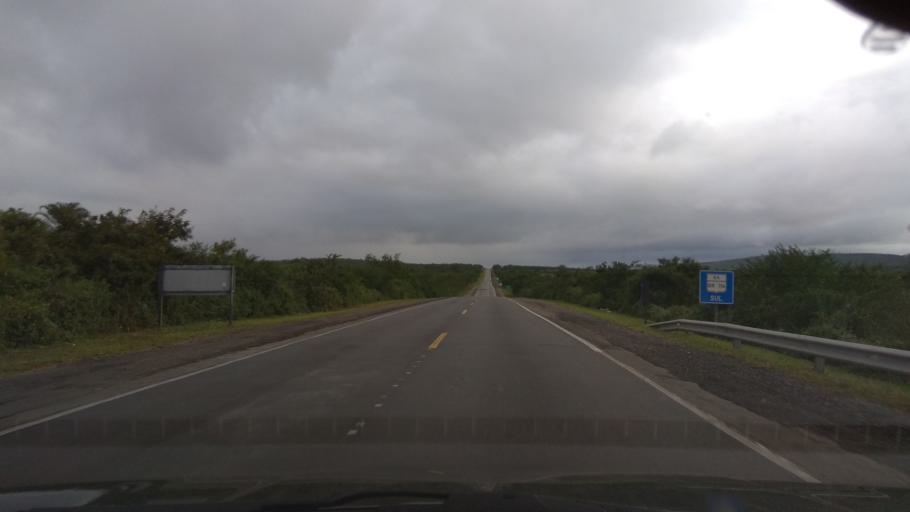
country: BR
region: Bahia
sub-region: Jaguaquara
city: Jaguaquara
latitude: -13.4109
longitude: -40.0254
